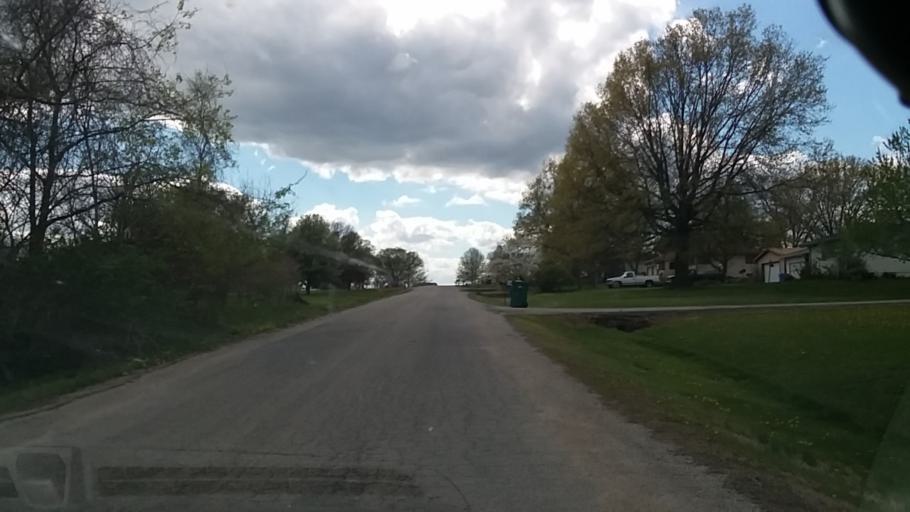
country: US
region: Kansas
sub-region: Douglas County
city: Lawrence
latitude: 38.8927
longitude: -95.2567
